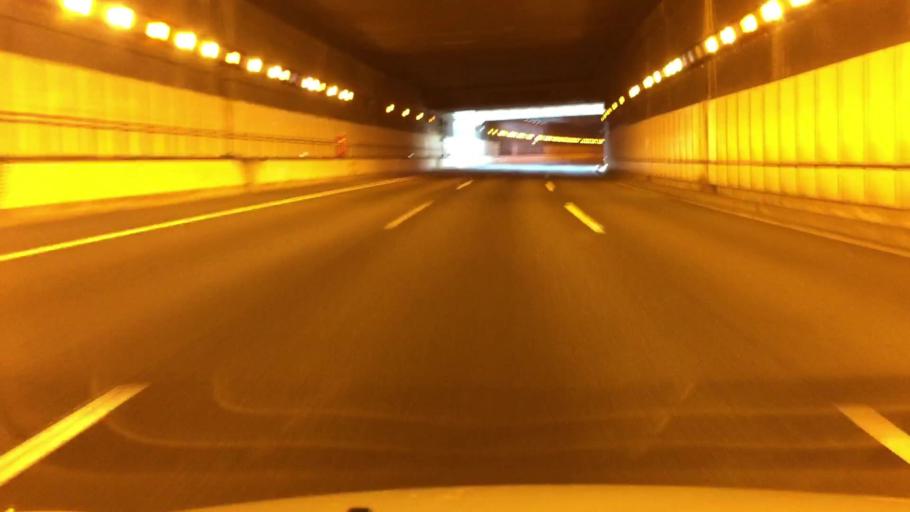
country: JP
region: Saitama
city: Wako
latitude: 35.7877
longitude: 139.6153
